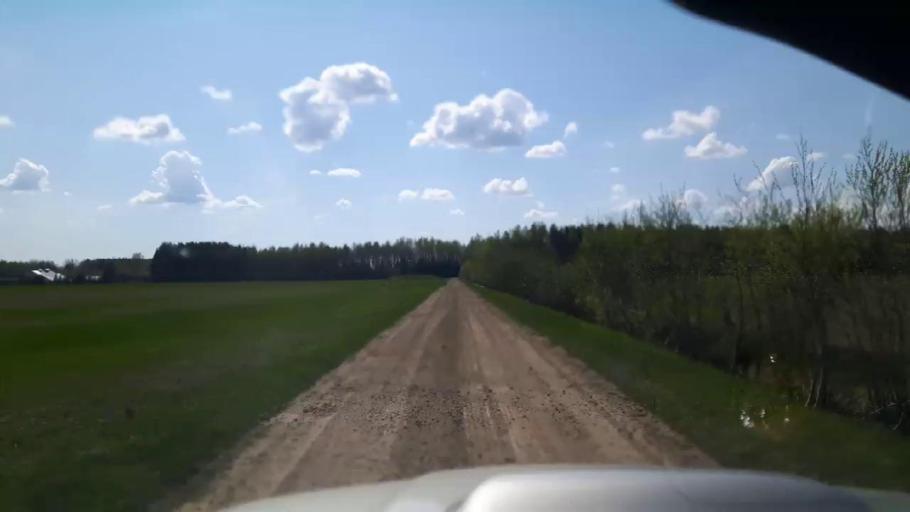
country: EE
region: Paernumaa
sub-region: Tootsi vald
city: Tootsi
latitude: 58.4997
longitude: 24.9403
